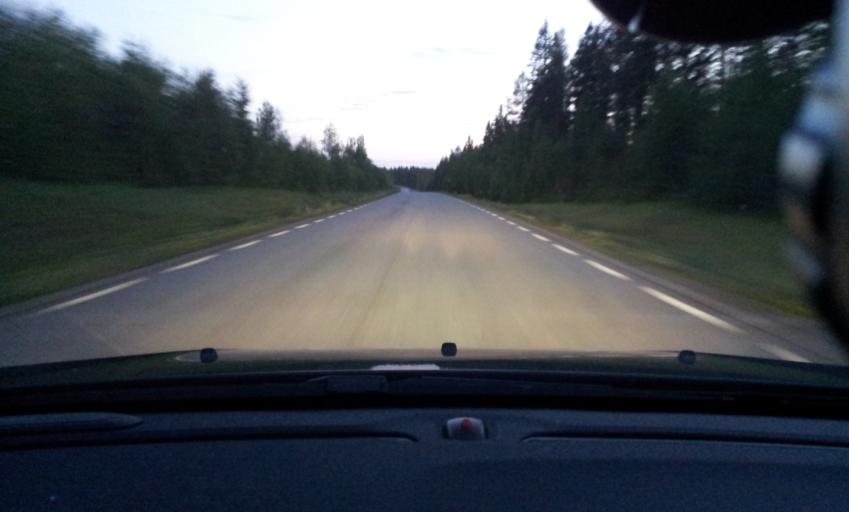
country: SE
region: Jaemtland
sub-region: Braecke Kommun
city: Braecke
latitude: 62.7507
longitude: 15.2666
